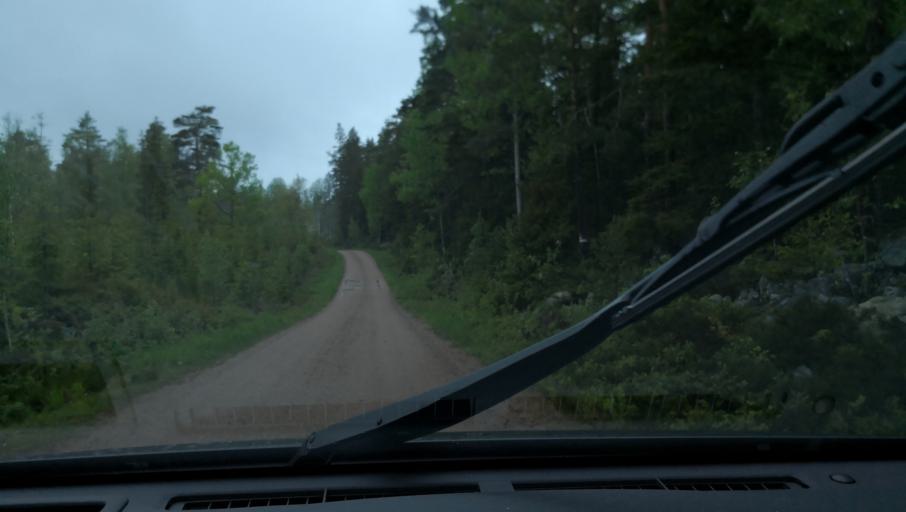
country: SE
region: Uppsala
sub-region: Enkopings Kommun
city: Orsundsbro
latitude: 59.9295
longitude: 17.3305
